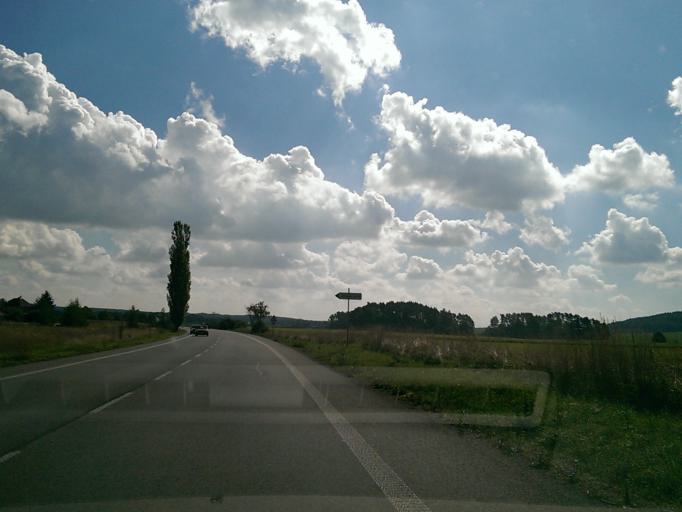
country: CZ
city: Doksy
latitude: 50.5587
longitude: 14.6541
